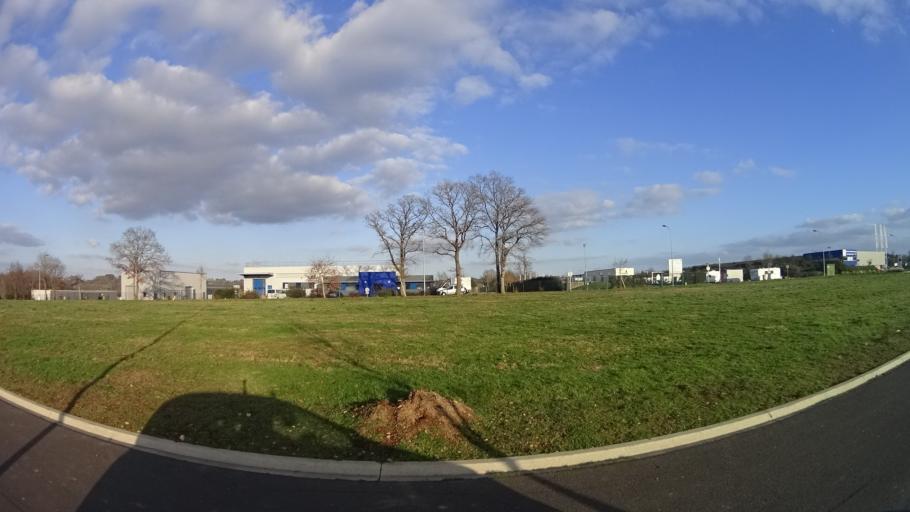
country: FR
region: Pays de la Loire
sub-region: Departement de la Loire-Atlantique
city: Saint-Nicolas-de-Redon
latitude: 47.6285
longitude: -2.0556
